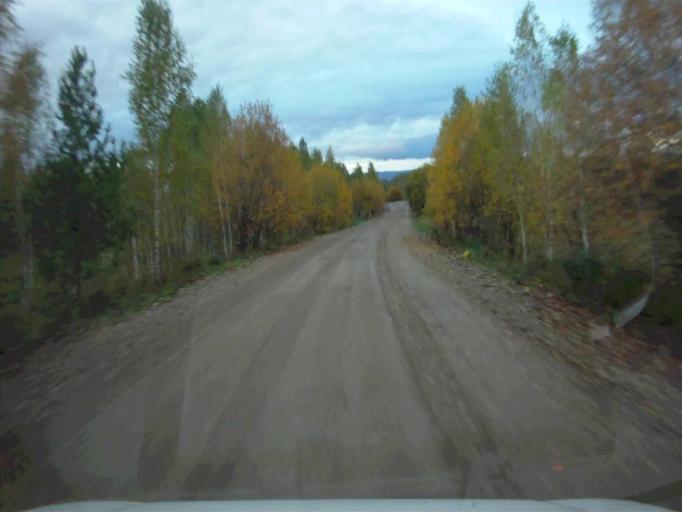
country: RU
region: Sverdlovsk
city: Mikhaylovsk
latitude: 56.2073
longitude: 59.2064
